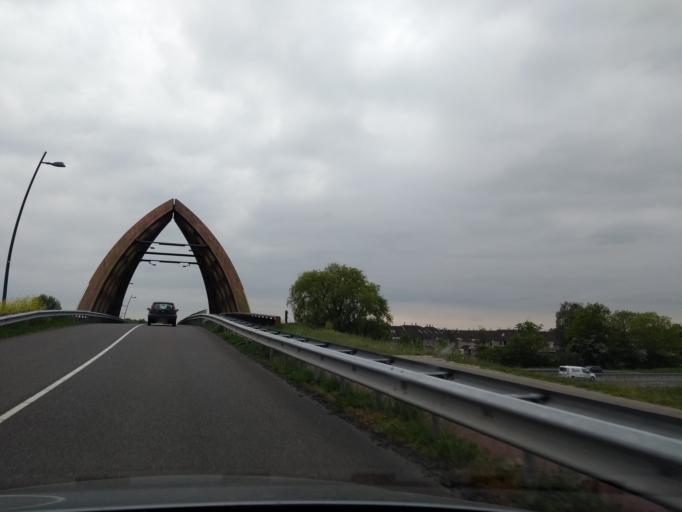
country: NL
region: Friesland
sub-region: Sudwest Fryslan
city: Sneek
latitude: 53.0225
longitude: 5.6626
